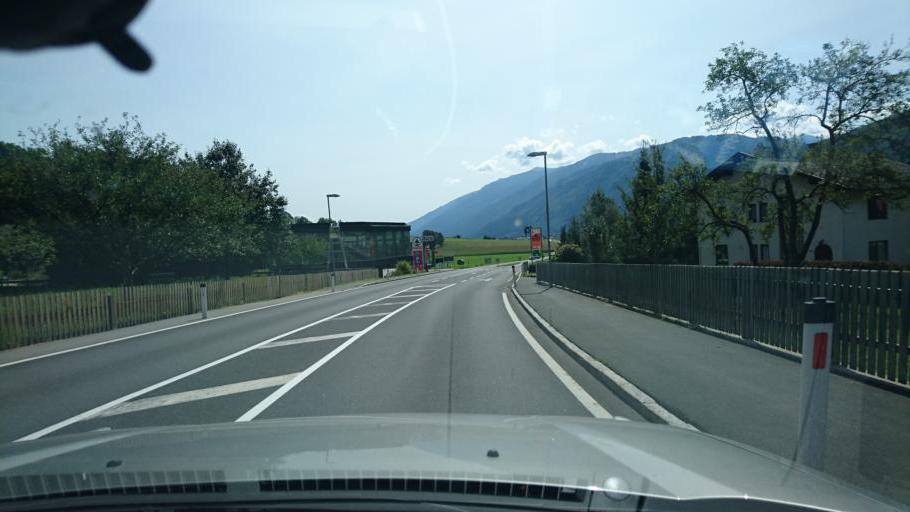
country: AT
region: Carinthia
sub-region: Politischer Bezirk Spittal an der Drau
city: Muhldorf
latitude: 46.8560
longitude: 13.3522
